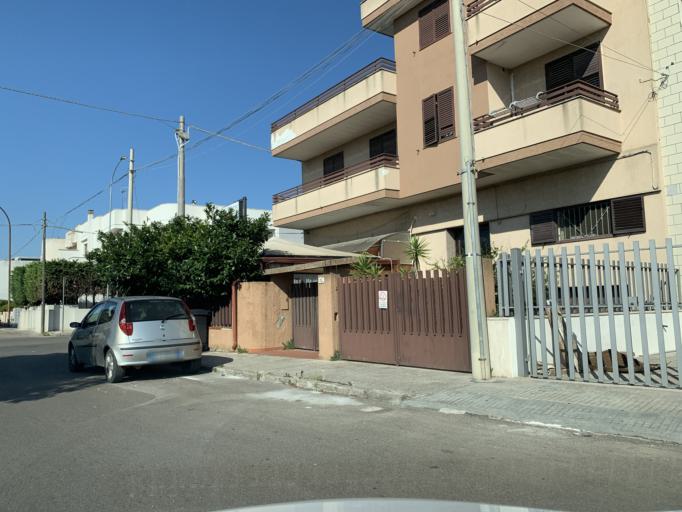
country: IT
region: Apulia
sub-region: Provincia di Lecce
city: Nardo
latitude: 40.1863
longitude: 18.0280
